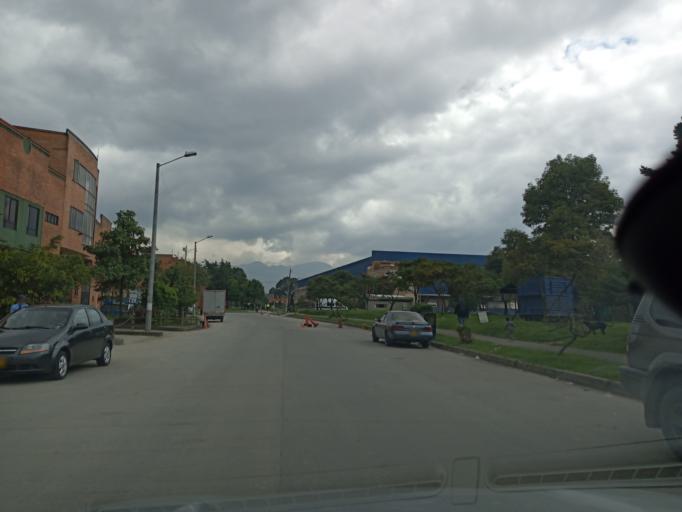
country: CO
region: Bogota D.C.
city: Bogota
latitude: 4.6522
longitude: -74.1184
